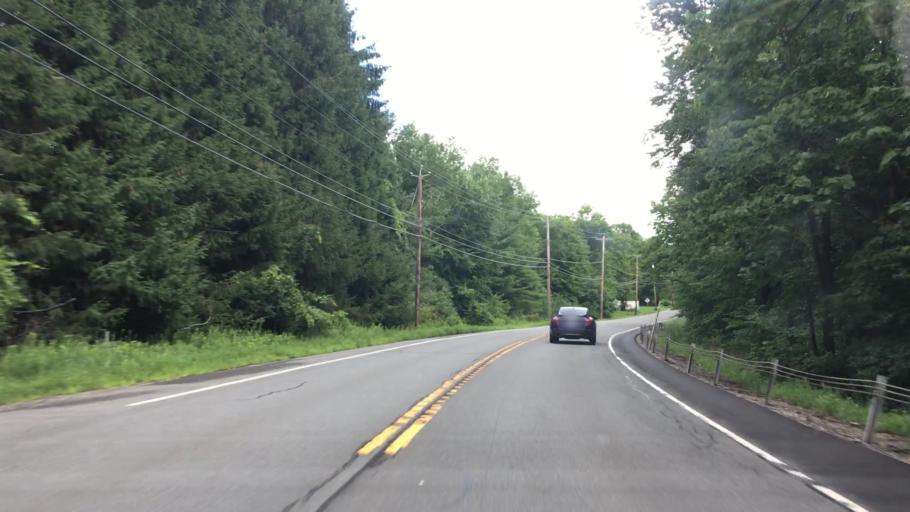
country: US
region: New York
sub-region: Rensselaer County
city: Poestenkill
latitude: 42.8240
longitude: -73.5037
